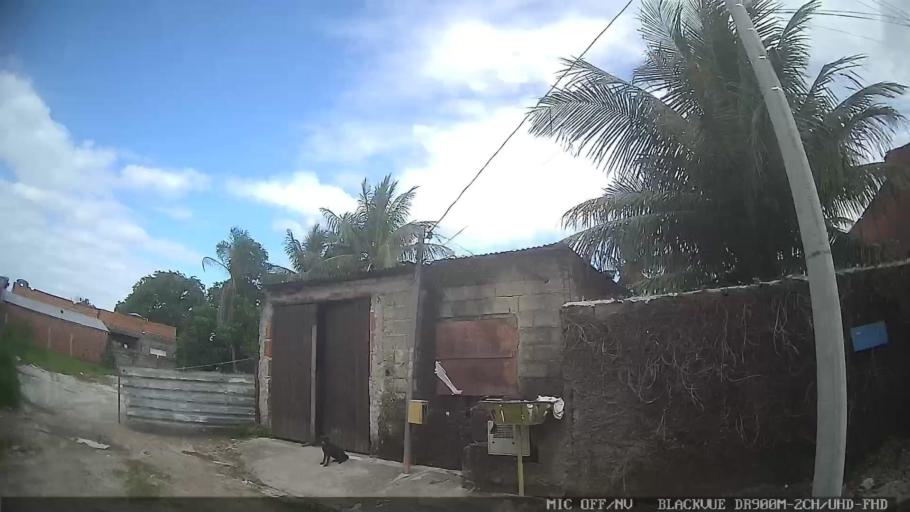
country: BR
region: Sao Paulo
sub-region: Sao Sebastiao
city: Sao Sebastiao
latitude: -23.7115
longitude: -45.4282
